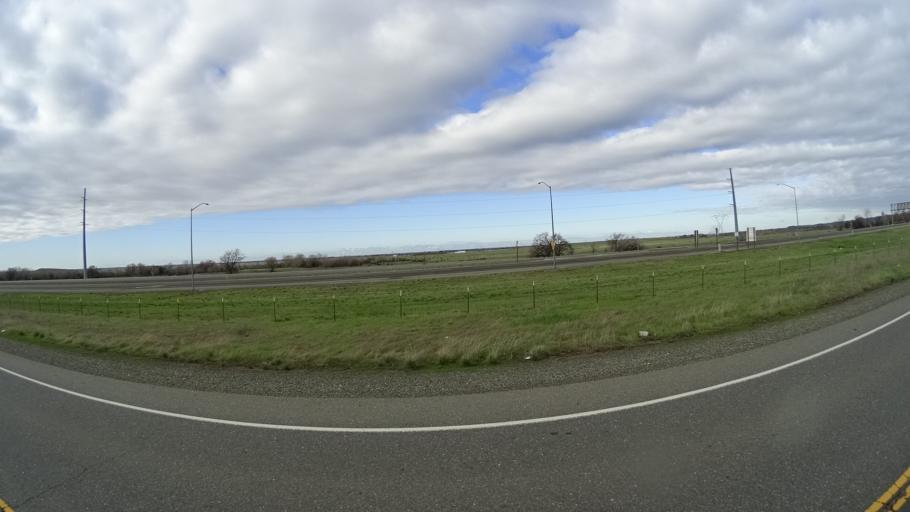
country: US
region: California
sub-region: Butte County
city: Thermalito
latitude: 39.5920
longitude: -121.6193
